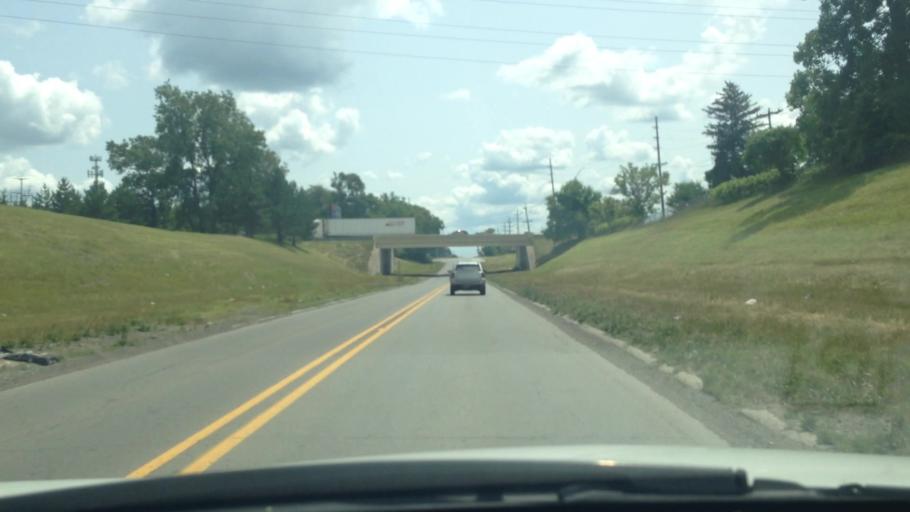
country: US
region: Michigan
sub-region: Wayne County
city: Taylor
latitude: 42.2486
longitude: -83.3084
